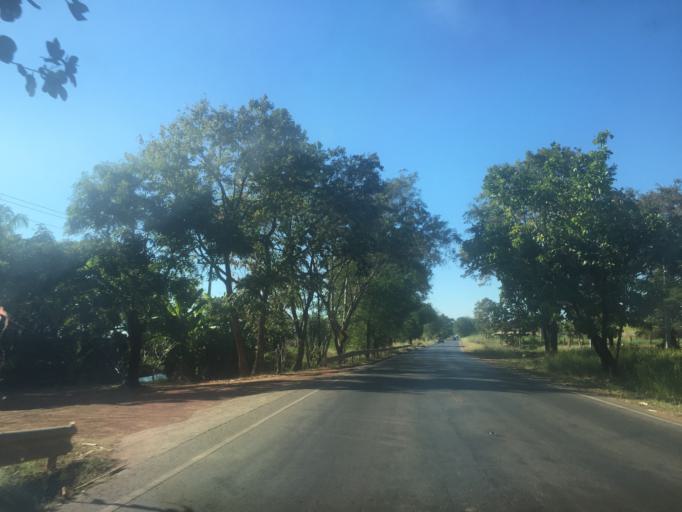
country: TH
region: Kalasin
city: Tha Khantho
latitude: 16.9642
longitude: 103.2478
